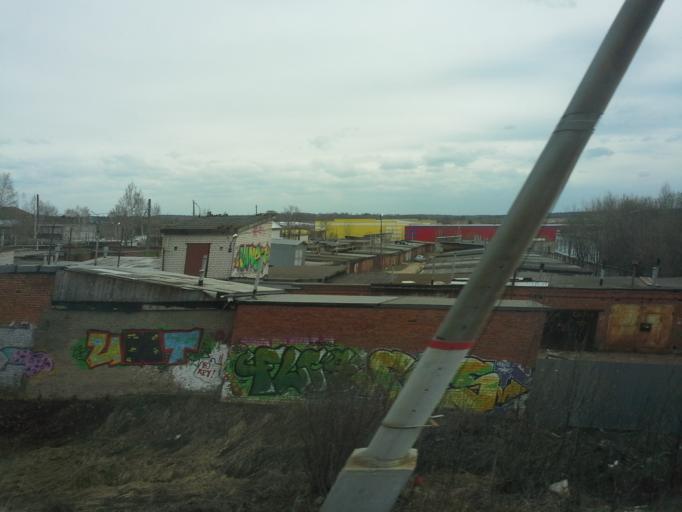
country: RU
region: Moskovskaya
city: Sergiyev Posad
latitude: 56.2891
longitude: 38.1153
